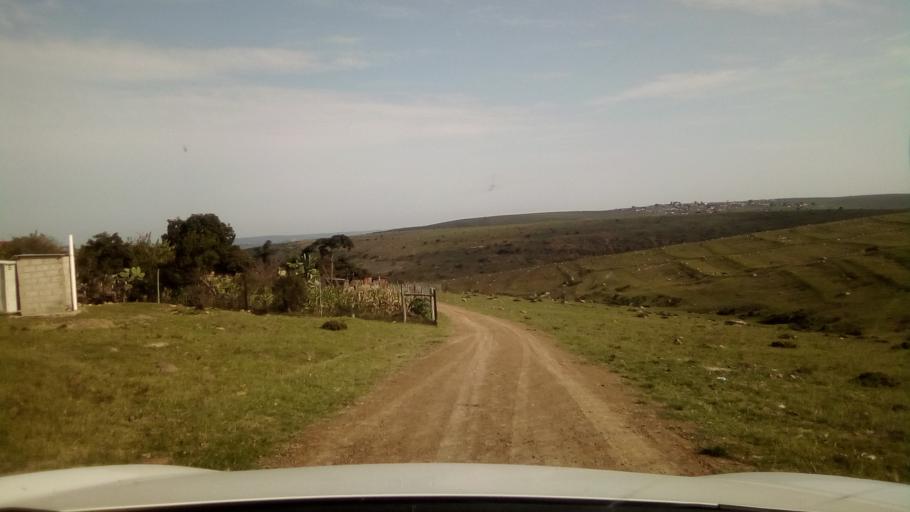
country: ZA
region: Eastern Cape
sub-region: Buffalo City Metropolitan Municipality
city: Bhisho
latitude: -33.0084
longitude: 27.3050
